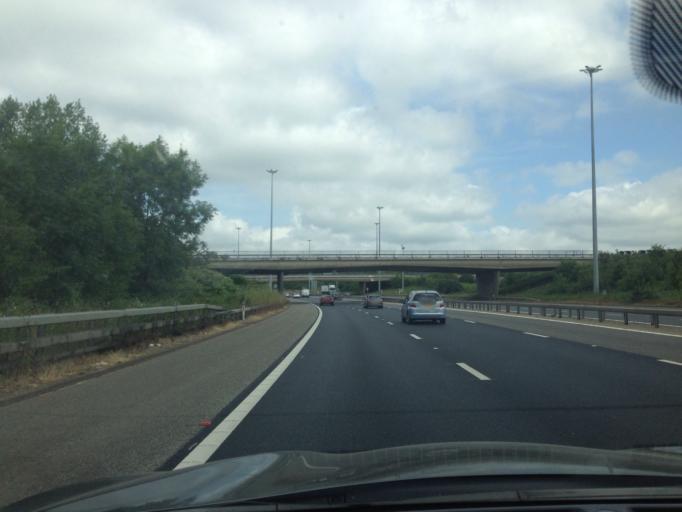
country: GB
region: England
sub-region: Greater London
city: Edgware
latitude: 51.6337
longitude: -0.2646
